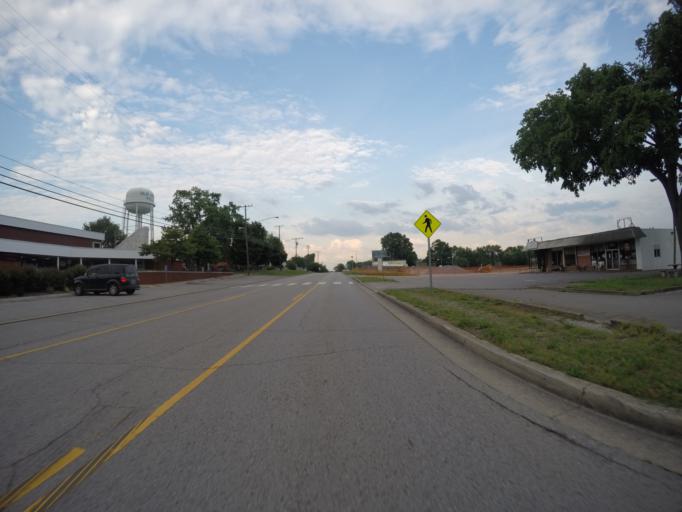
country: US
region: Tennessee
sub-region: Davidson County
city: Lakewood
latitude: 36.2641
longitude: -86.6495
